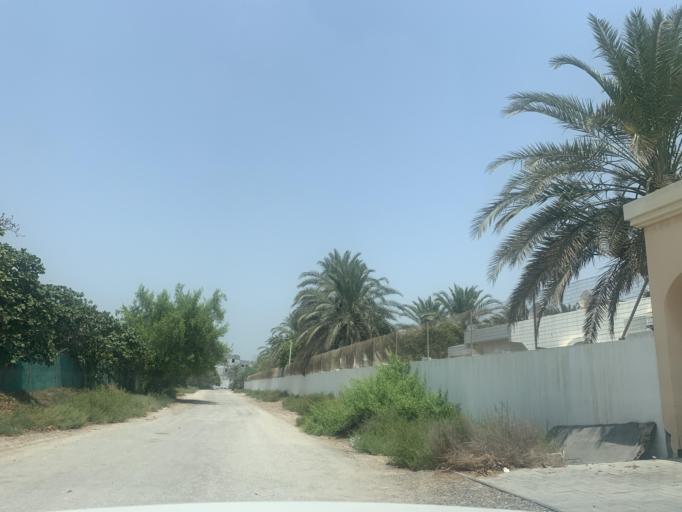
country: BH
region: Central Governorate
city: Madinat Hamad
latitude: 26.1479
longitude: 50.4629
